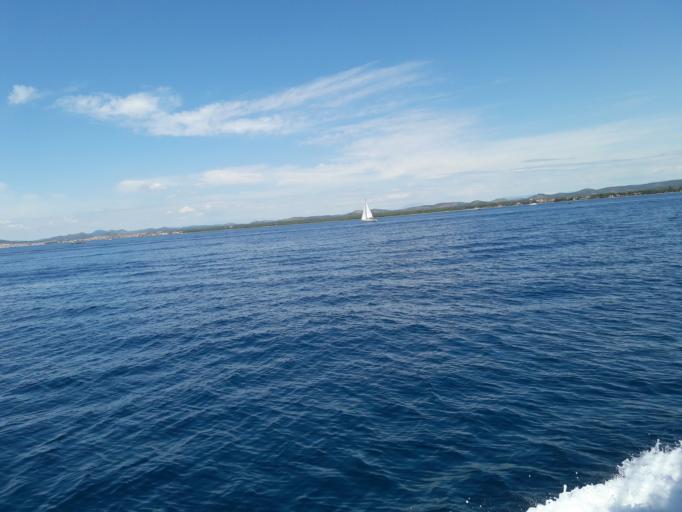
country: HR
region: Sibensko-Kniniska
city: Vodice
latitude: 43.7075
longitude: 15.8309
